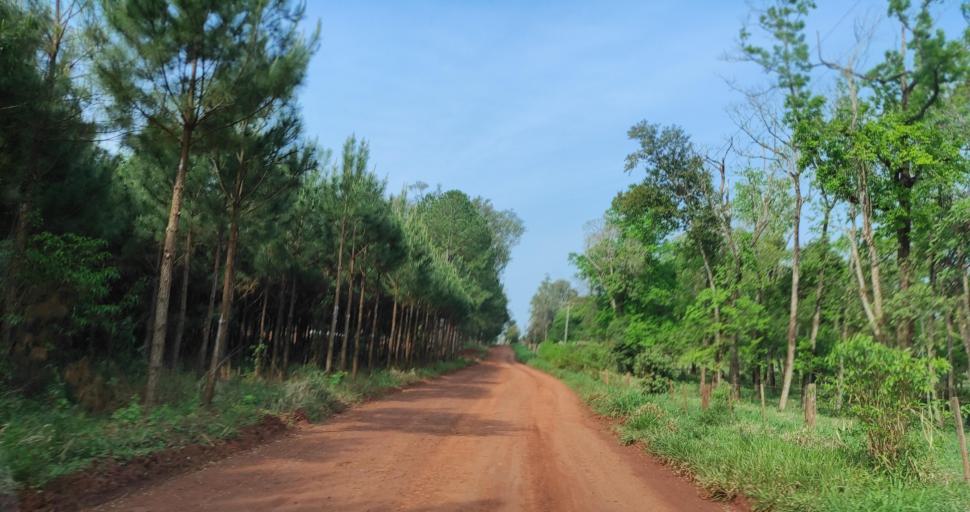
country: AR
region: Misiones
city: Garuhape
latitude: -26.8664
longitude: -54.9980
